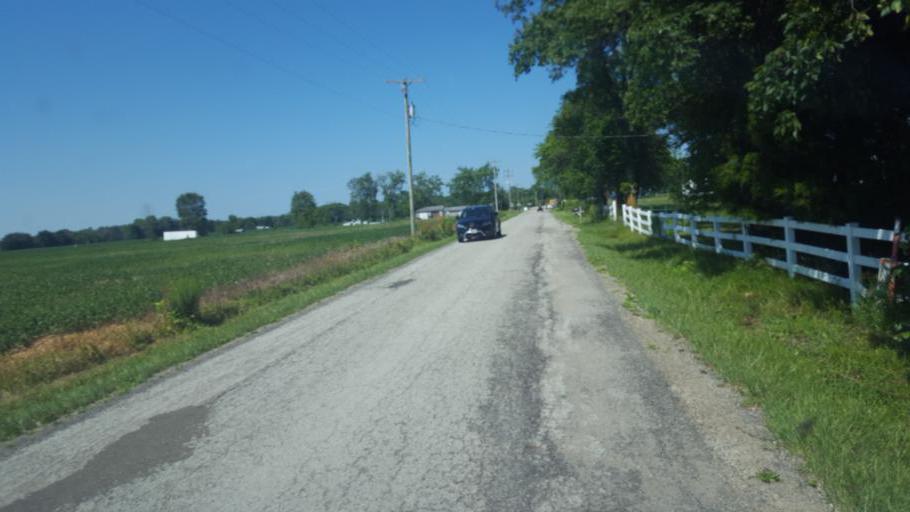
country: US
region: Ohio
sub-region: Delaware County
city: Ashley
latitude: 40.4535
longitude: -82.9487
